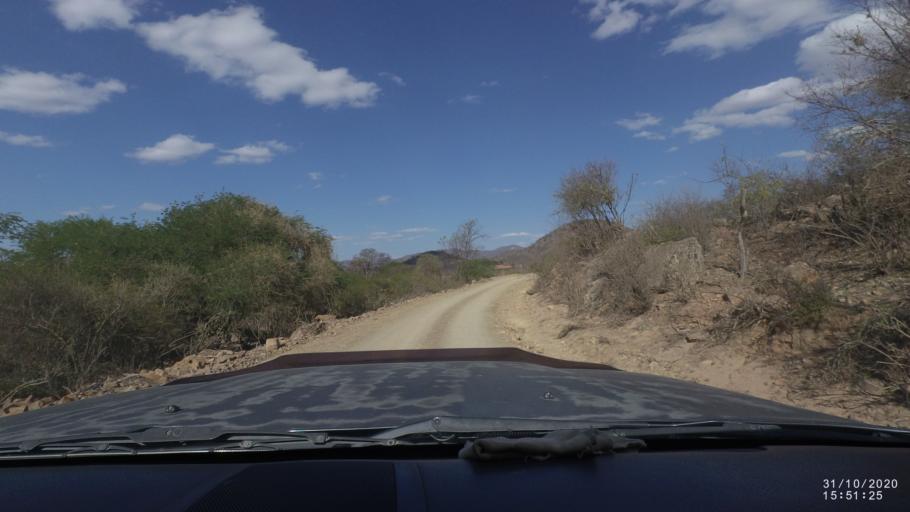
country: BO
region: Chuquisaca
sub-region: Provincia Zudanez
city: Mojocoya
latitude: -18.3163
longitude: -64.7035
